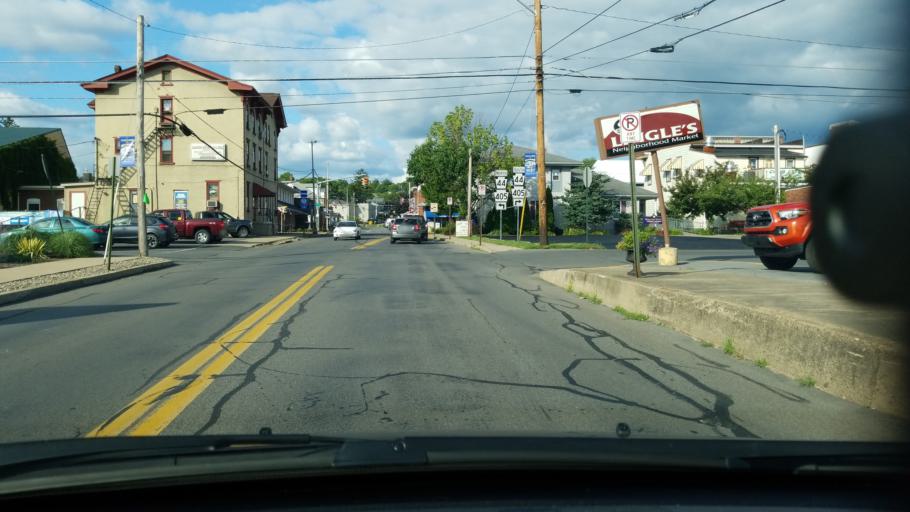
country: US
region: Pennsylvania
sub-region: Northumberland County
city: Watsontown
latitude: 41.0822
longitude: -76.8625
